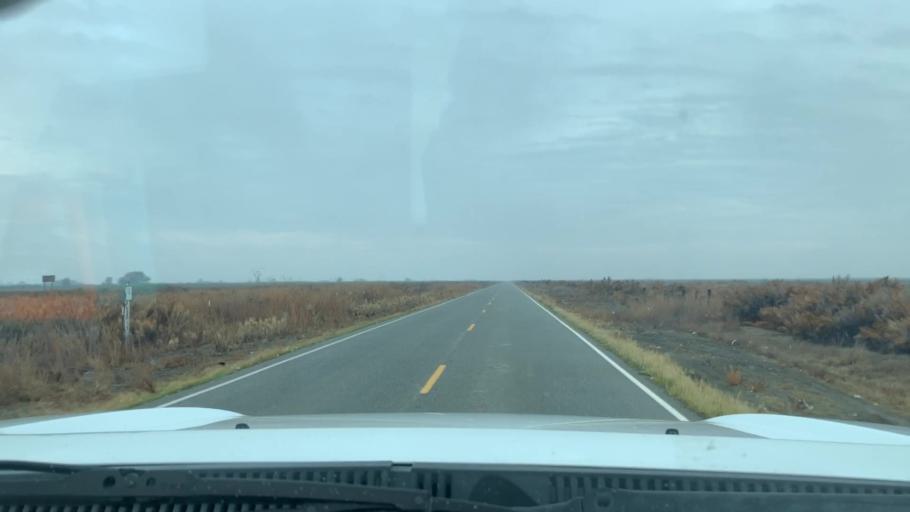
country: US
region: California
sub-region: Kern County
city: Lost Hills
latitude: 35.7335
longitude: -119.5794
